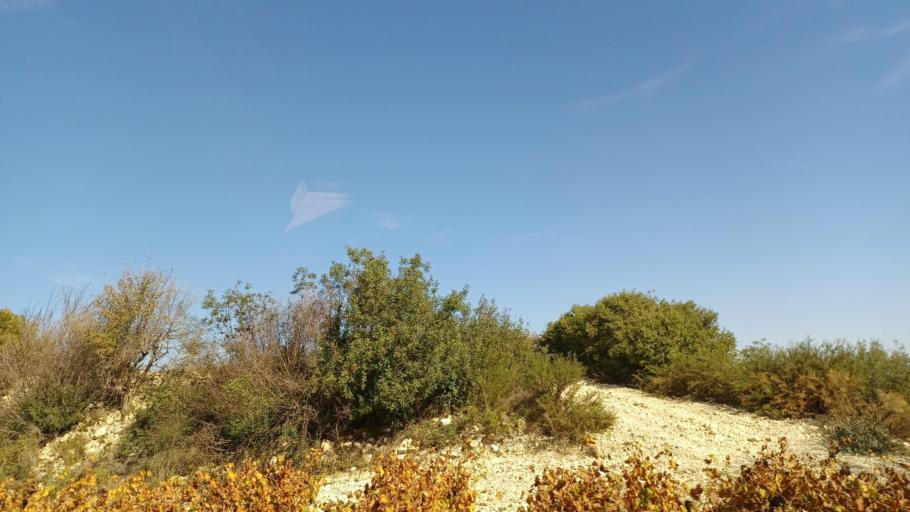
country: CY
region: Pafos
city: Pegeia
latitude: 34.9339
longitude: 32.4481
